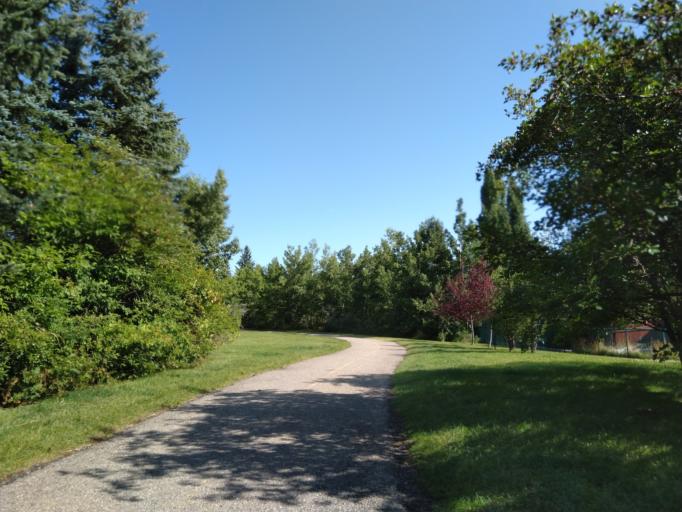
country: CA
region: Alberta
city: Calgary
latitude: 51.0955
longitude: -114.2437
